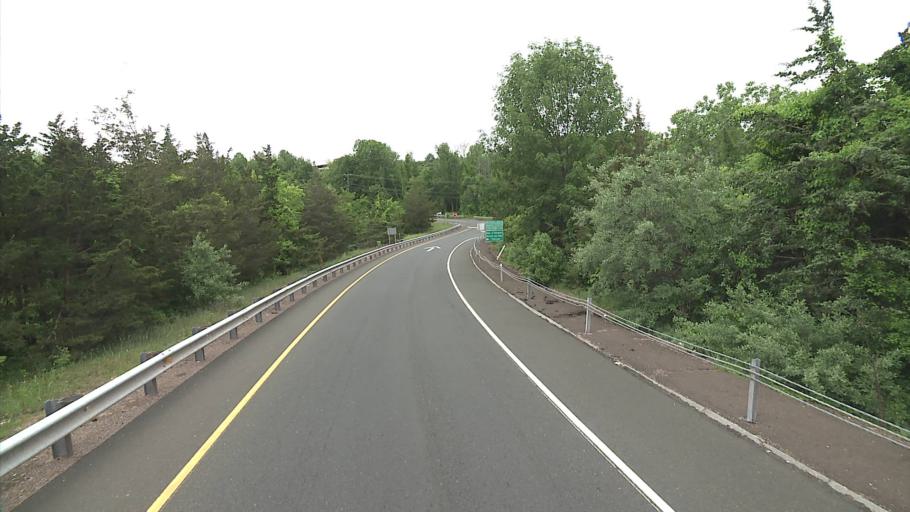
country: US
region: Connecticut
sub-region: Middlesex County
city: Middletown
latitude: 41.5720
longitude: -72.7248
